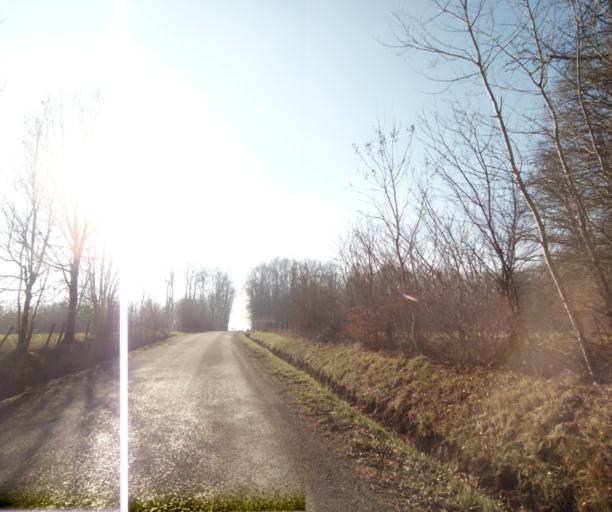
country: FR
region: Champagne-Ardenne
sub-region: Departement de la Haute-Marne
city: Wassy
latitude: 48.5090
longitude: 4.9640
